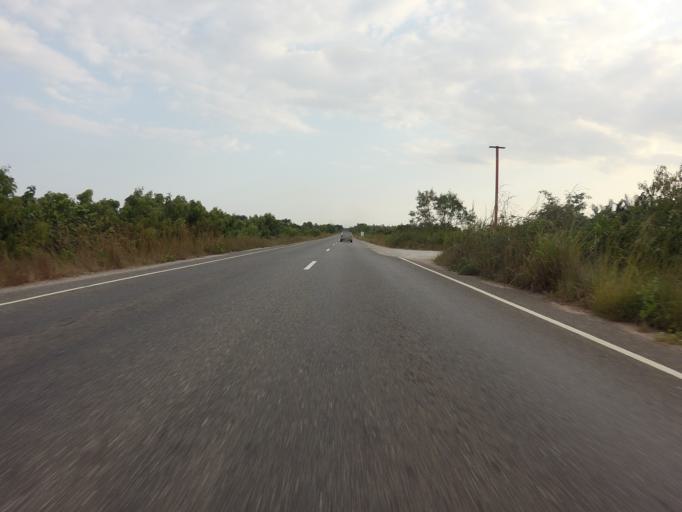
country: GH
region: Volta
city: Ho
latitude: 6.1284
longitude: 0.5230
